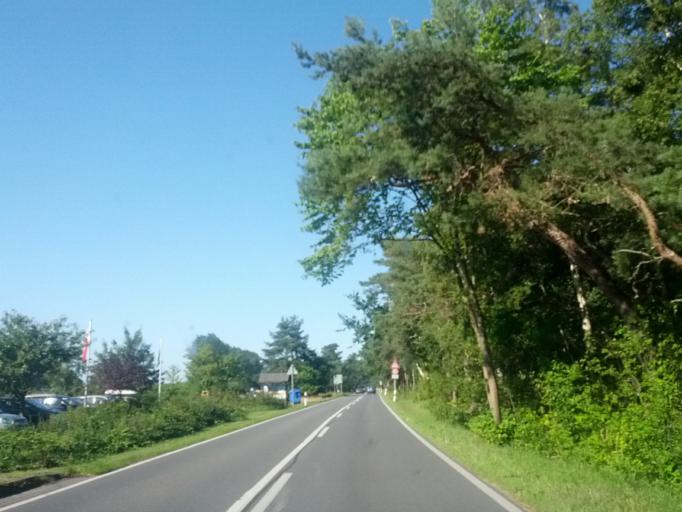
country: DE
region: Mecklenburg-Vorpommern
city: Ostseebad Gohren
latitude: 54.3029
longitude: 13.7144
